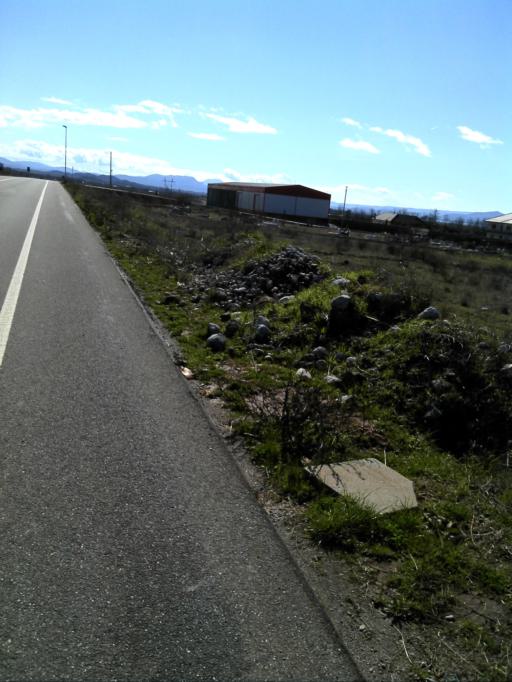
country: AL
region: Shkoder
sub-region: Rrethi i Malesia e Madhe
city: Koplik
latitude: 42.2125
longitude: 19.4542
